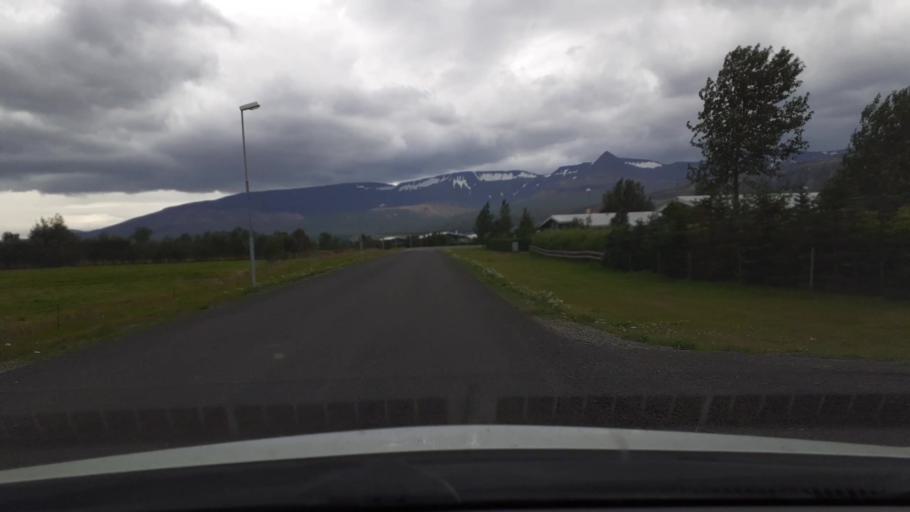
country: IS
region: West
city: Borgarnes
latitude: 64.5642
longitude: -21.7618
